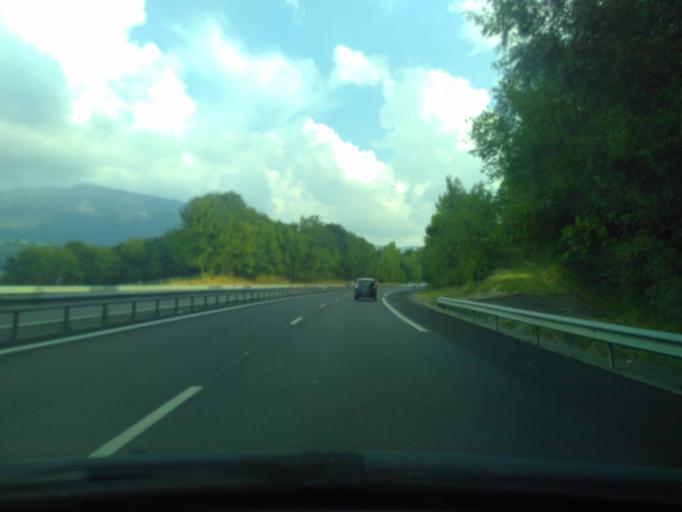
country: FR
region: Rhone-Alpes
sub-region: Departement de la Haute-Savoie
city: Etaux
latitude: 46.0602
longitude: 6.2919
